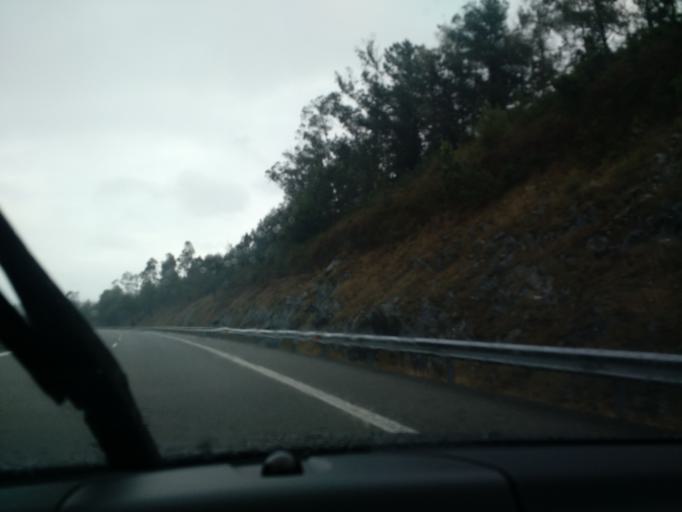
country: ES
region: Galicia
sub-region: Provincia da Coruna
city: Abegondo
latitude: 43.1696
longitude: -8.3190
